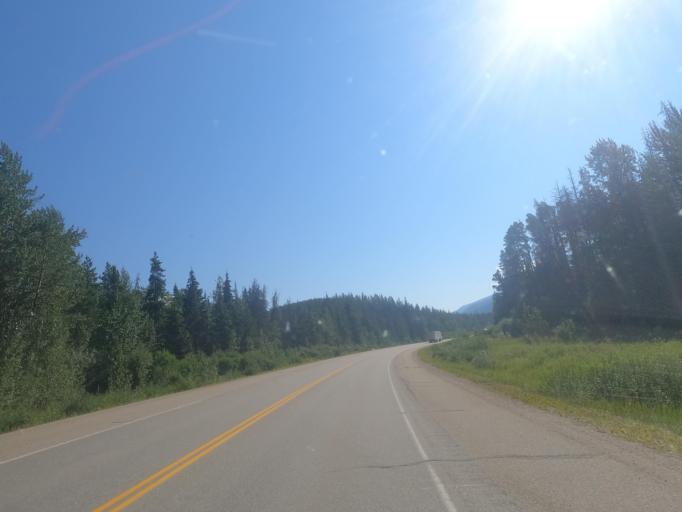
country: CA
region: Alberta
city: Jasper Park Lodge
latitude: 52.8881
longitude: -118.4750
